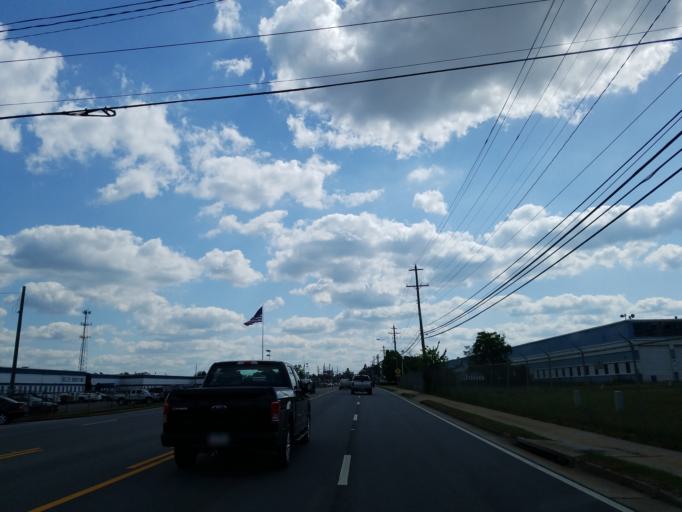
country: US
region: Georgia
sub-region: Peach County
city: Fort Valley
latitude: 32.5614
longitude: -83.8810
